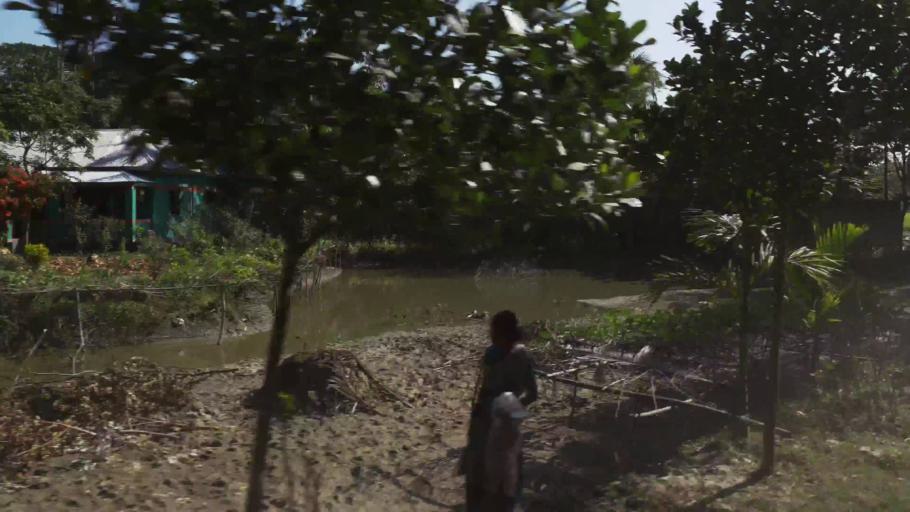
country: BD
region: Dhaka
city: Gafargaon
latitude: 24.5340
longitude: 90.5086
